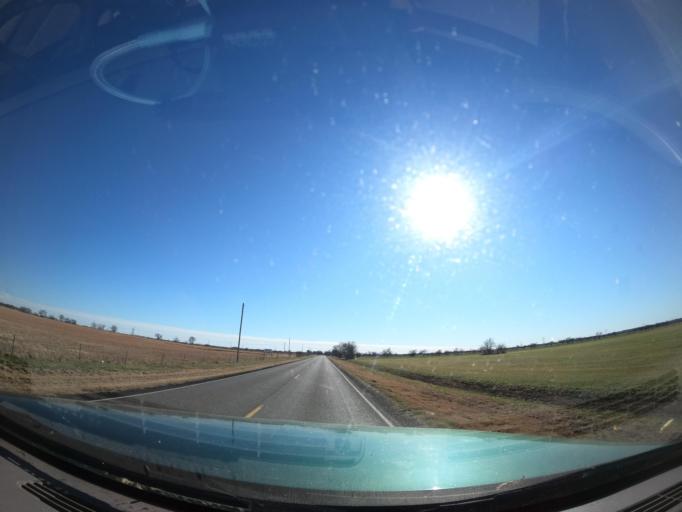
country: US
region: Oklahoma
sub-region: McIntosh County
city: Checotah
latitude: 35.5839
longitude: -95.6599
